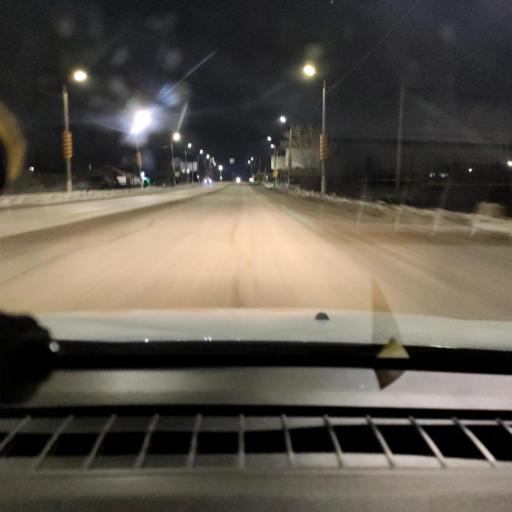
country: RU
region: Samara
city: Novokuybyshevsk
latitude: 53.0814
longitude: 49.9599
